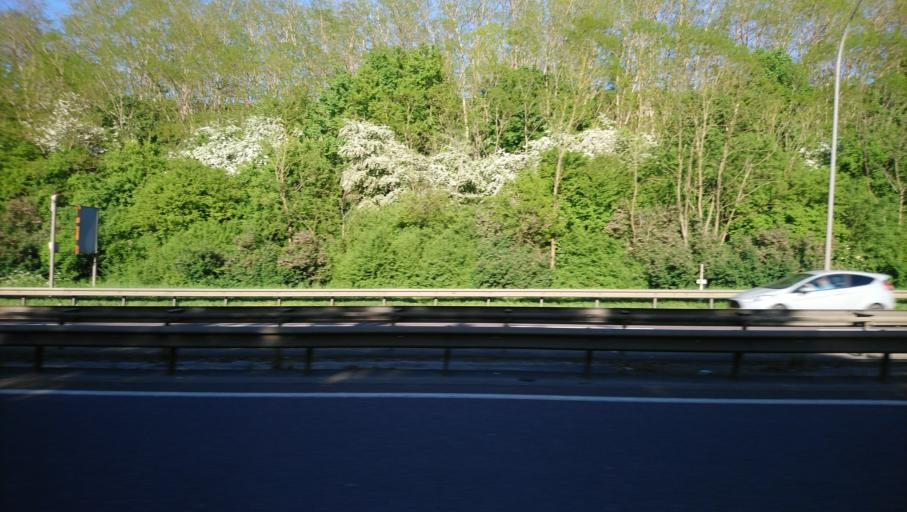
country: LU
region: Luxembourg
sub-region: Canton d'Esch-sur-Alzette
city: Leudelange
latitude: 49.5800
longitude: 6.0877
